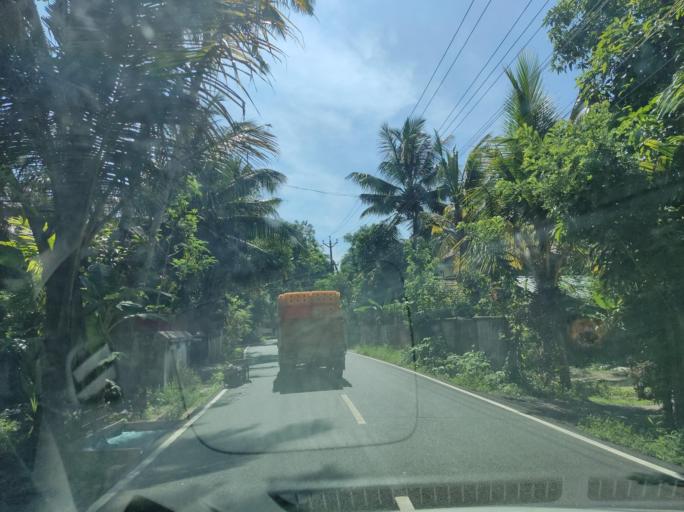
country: IN
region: Kerala
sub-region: Alappuzha
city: Kayankulam
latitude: 9.2655
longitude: 76.4072
